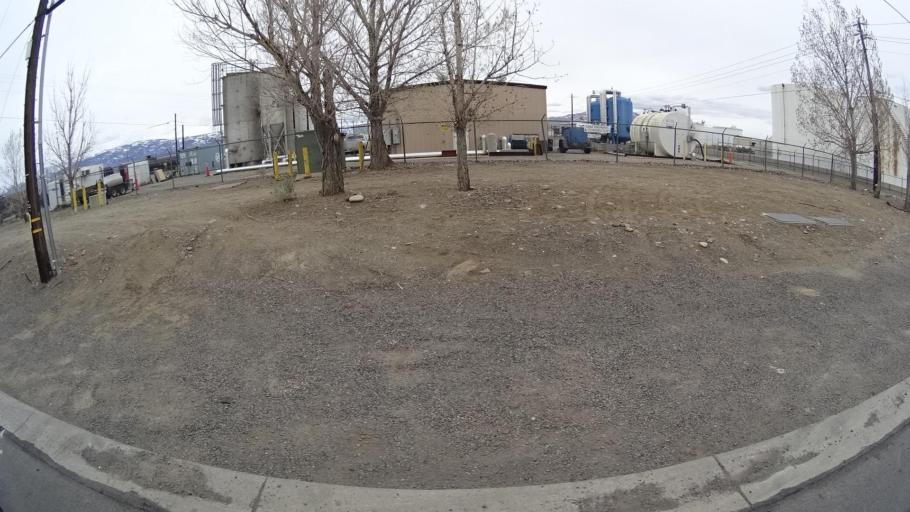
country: US
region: Nevada
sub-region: Washoe County
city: Sparks
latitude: 39.5317
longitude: -119.7434
